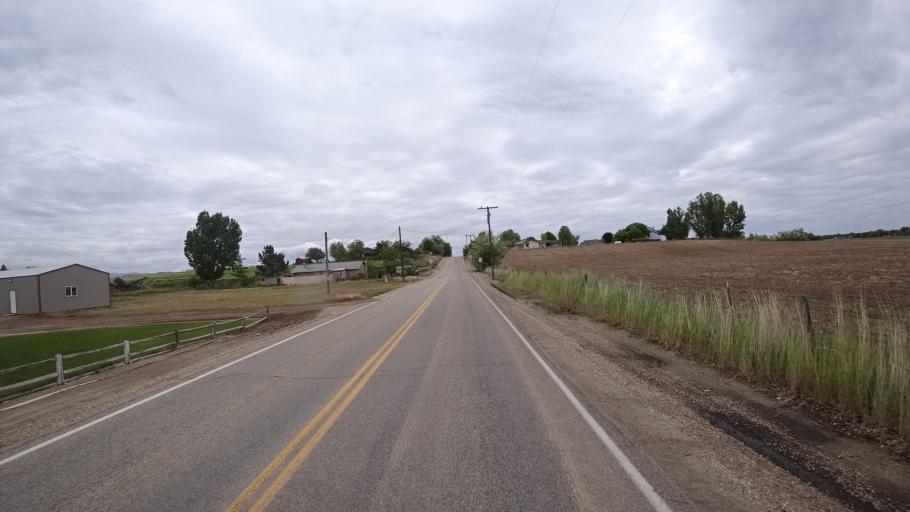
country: US
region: Idaho
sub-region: Ada County
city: Star
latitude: 43.7101
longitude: -116.4677
